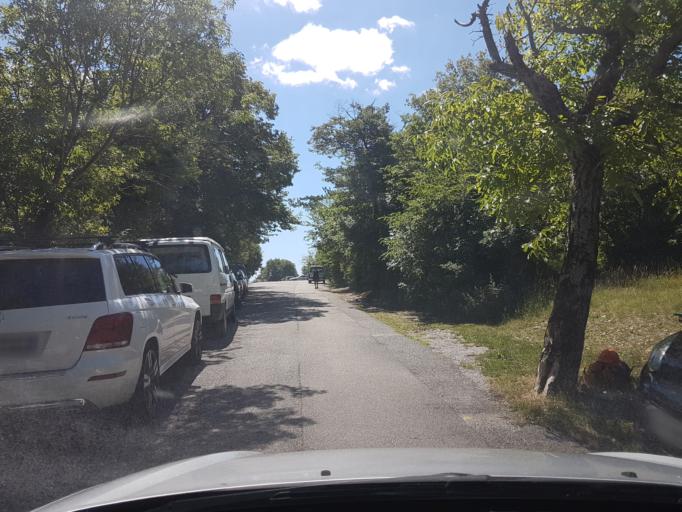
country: IT
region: Friuli Venezia Giulia
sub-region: Provincia di Trieste
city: Prosecco-Contovello
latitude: 45.6986
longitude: 13.7411
